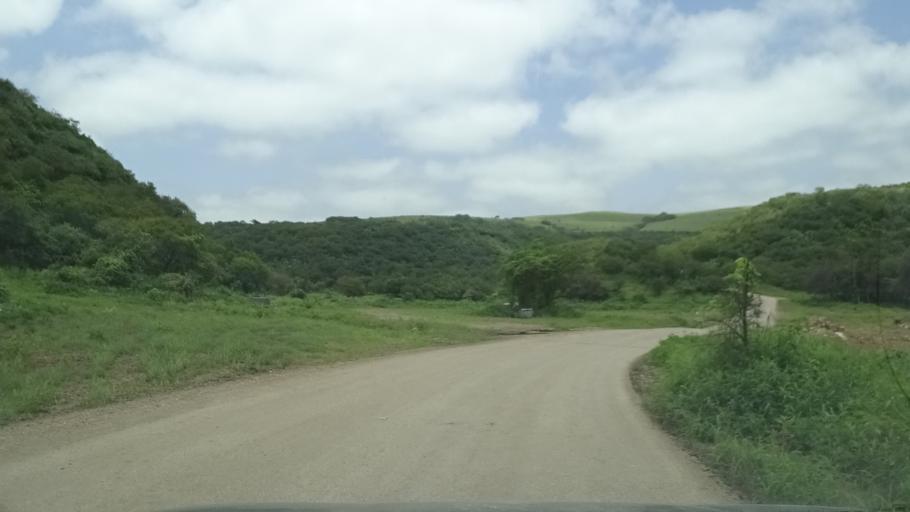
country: OM
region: Zufar
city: Salalah
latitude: 17.1976
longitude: 54.1815
